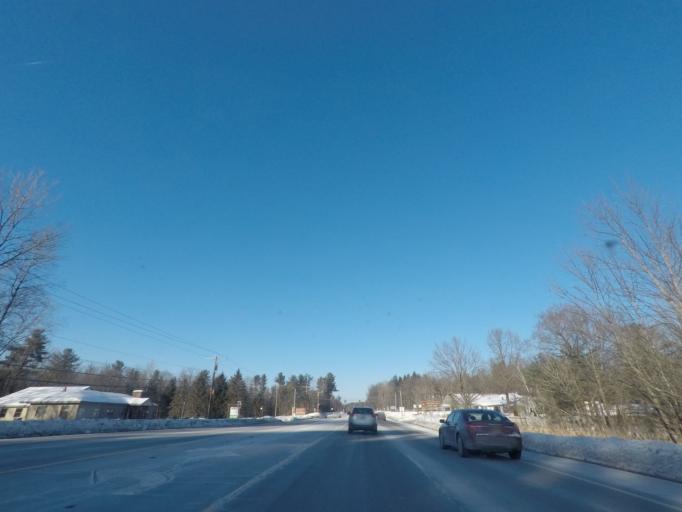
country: US
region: New York
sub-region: Saratoga County
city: Saratoga Springs
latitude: 43.0444
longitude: -73.7904
